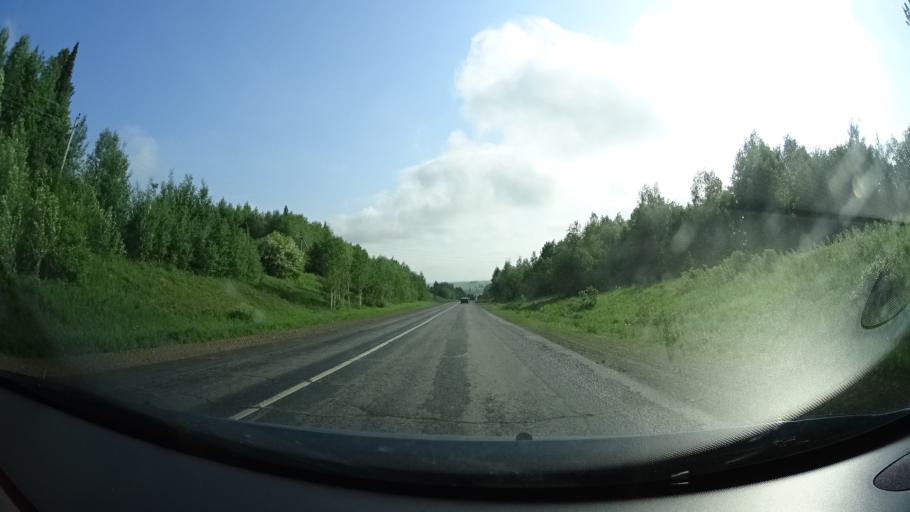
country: RU
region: Perm
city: Kultayevo
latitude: 57.8453
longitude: 55.8311
